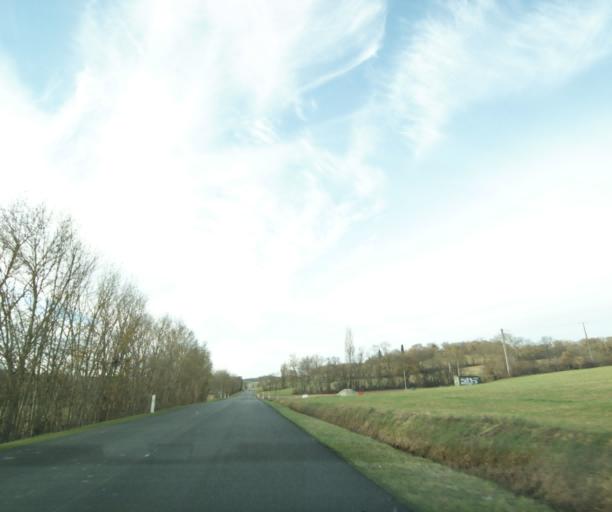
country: FR
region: Midi-Pyrenees
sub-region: Departement du Gers
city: Jegun
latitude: 43.6827
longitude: 0.4940
